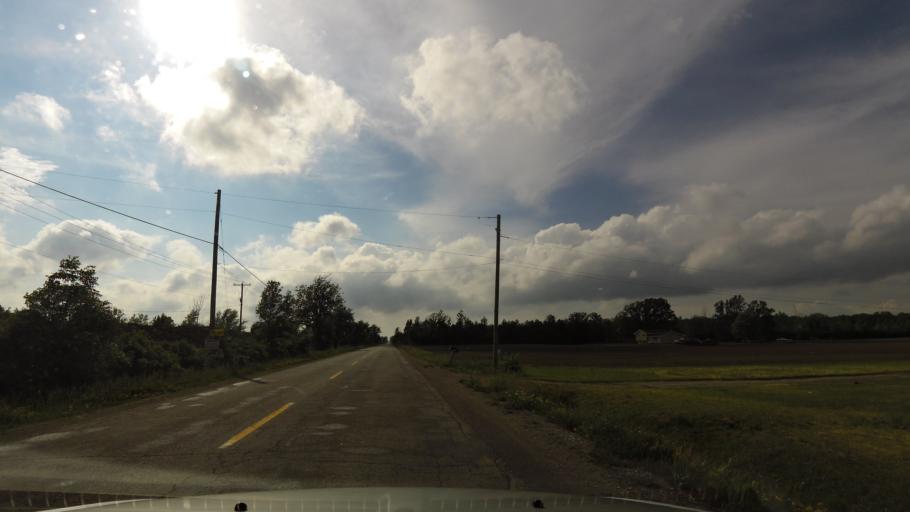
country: CA
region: Ontario
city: Ancaster
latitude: 43.0196
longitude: -80.0407
